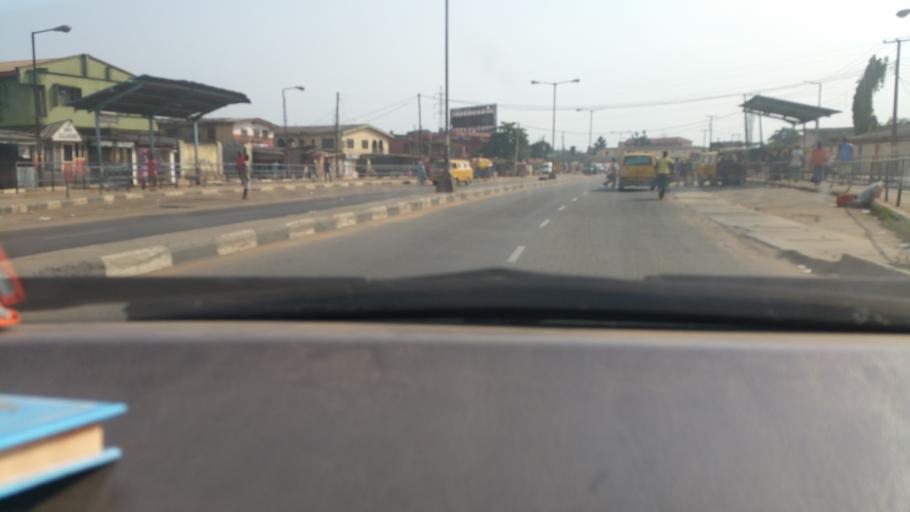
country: NG
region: Lagos
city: Ikotun
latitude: 6.5798
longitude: 3.2838
